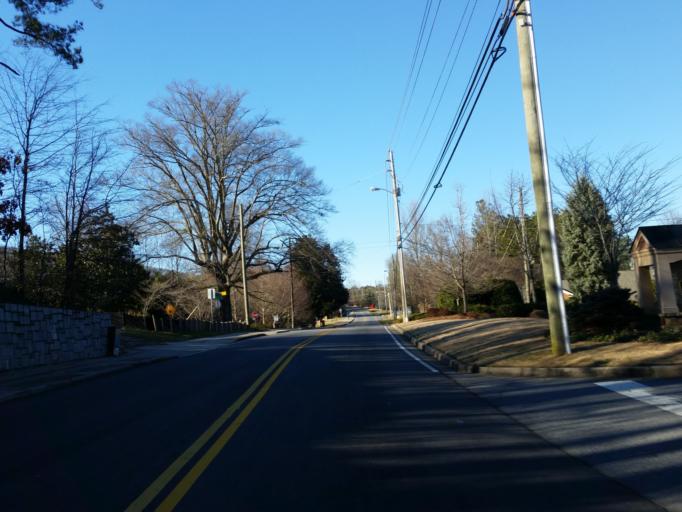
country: US
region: Georgia
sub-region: Cobb County
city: Marietta
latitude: 33.9705
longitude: -84.5635
